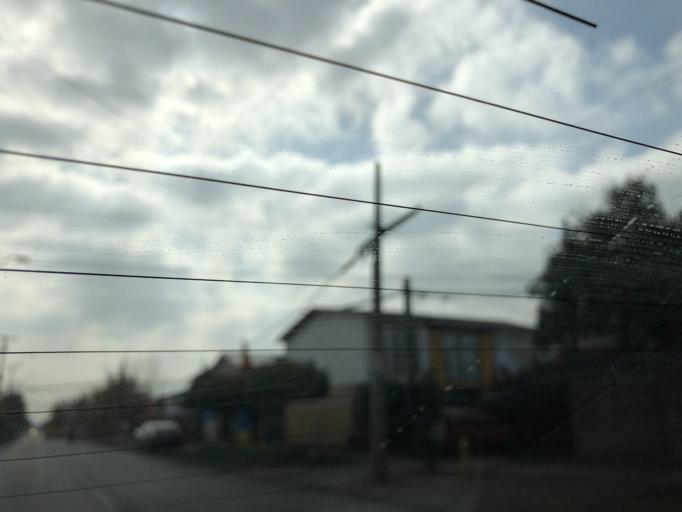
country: CL
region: Santiago Metropolitan
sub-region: Provincia de Cordillera
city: Puente Alto
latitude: -33.5859
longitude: -70.5914
